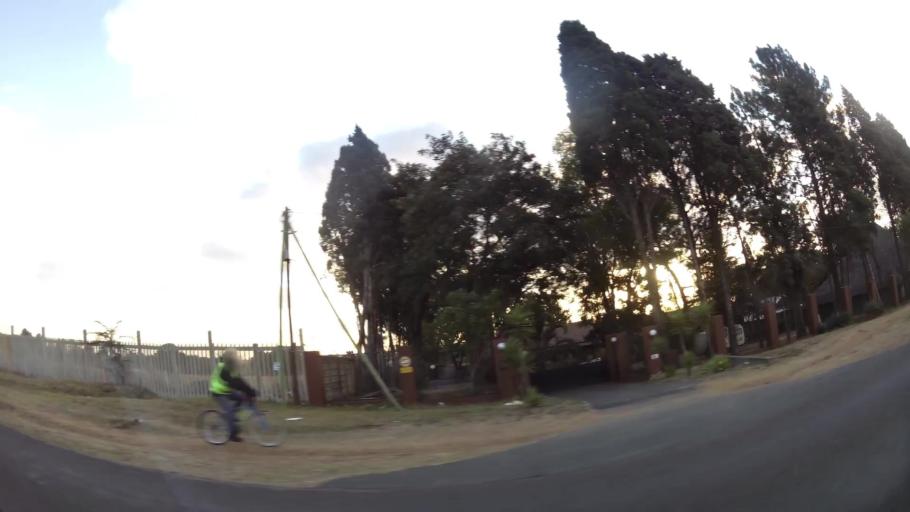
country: ZA
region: Gauteng
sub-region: City of Johannesburg Metropolitan Municipality
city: Midrand
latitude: -25.9850
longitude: 28.1528
